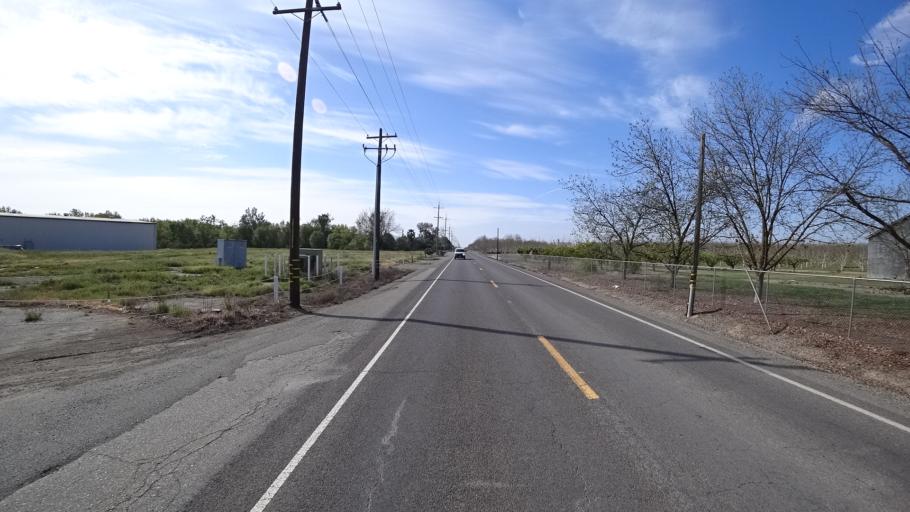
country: US
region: California
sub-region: Glenn County
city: Hamilton City
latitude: 39.6286
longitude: -122.0069
